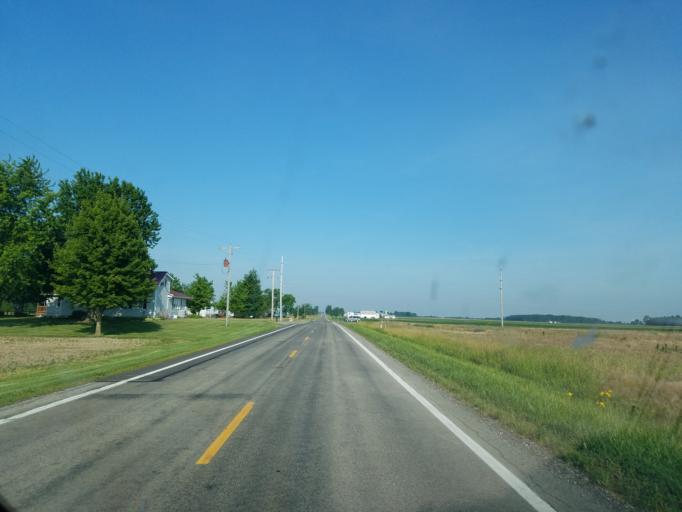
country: US
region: Ohio
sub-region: Hardin County
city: Kenton
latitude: 40.7320
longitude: -83.6509
